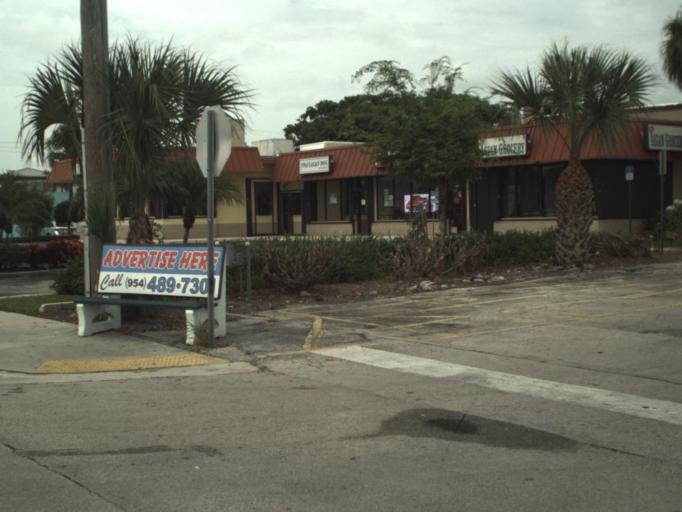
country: US
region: Florida
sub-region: Broward County
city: Deerfield Beach
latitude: 26.3061
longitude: -80.0928
